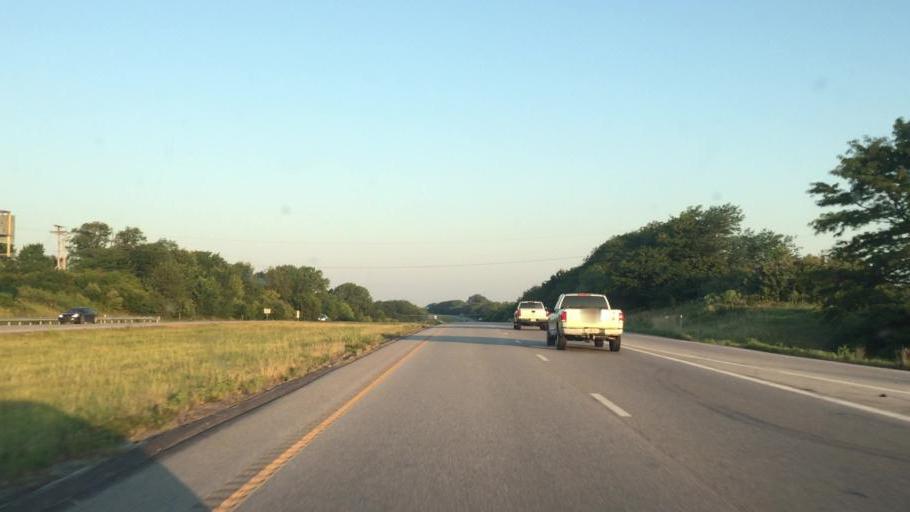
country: US
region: Missouri
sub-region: Clay County
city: Smithville
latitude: 39.3114
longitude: -94.5599
